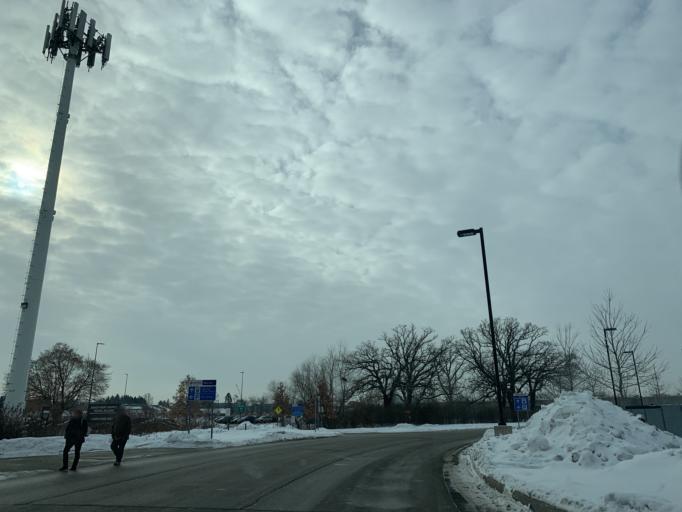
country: US
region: Minnesota
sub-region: Dakota County
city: Mendota Heights
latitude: 44.8927
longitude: -93.1950
